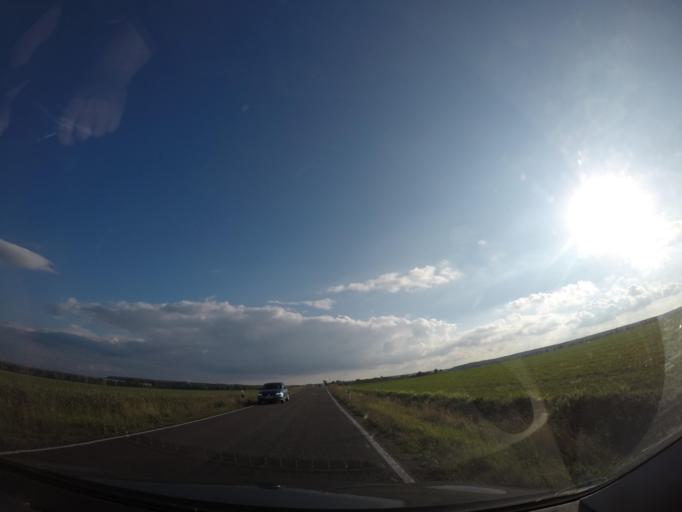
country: DE
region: Saxony-Anhalt
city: Weferlingen
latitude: 52.3310
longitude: 11.0668
